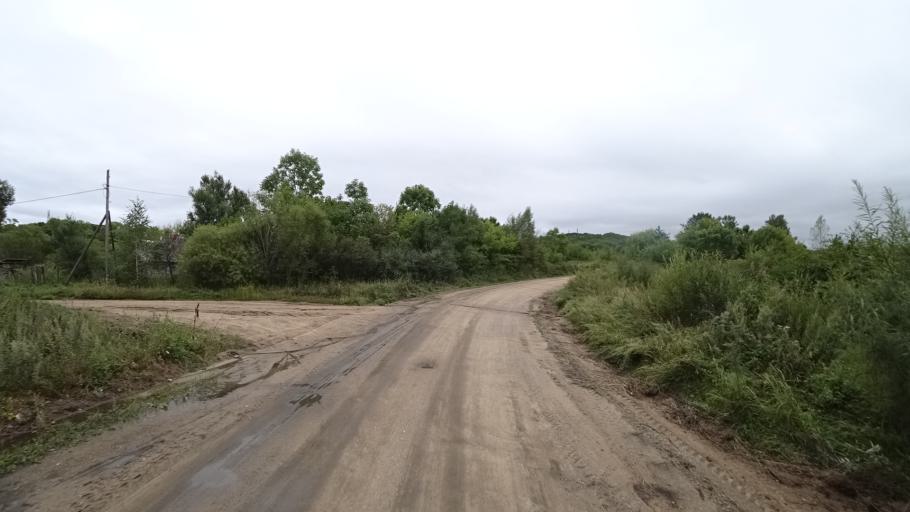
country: RU
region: Primorskiy
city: Rettikhovka
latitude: 44.1653
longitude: 132.7423
